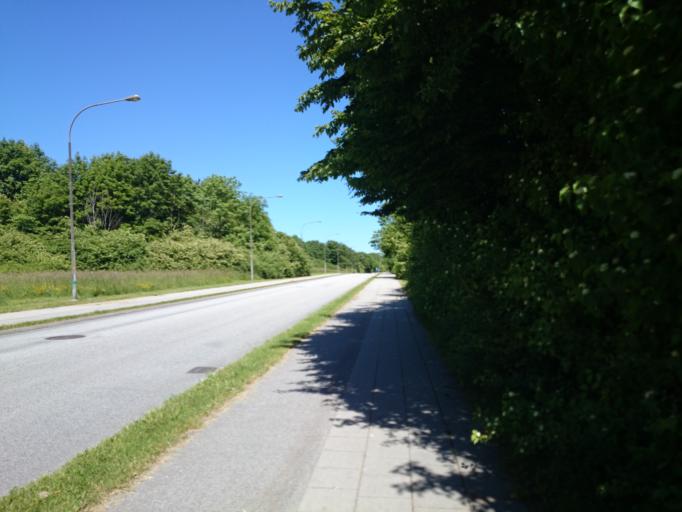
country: SE
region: Skane
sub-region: Lunds Kommun
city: Lund
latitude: 55.7112
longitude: 13.2222
